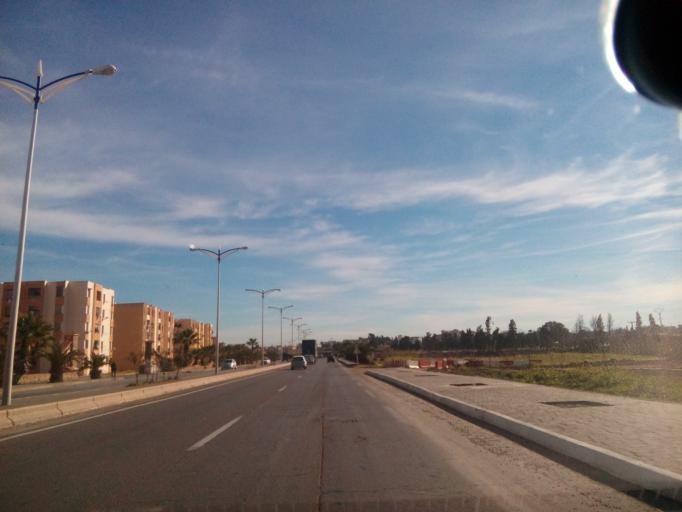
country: DZ
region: Mostaganem
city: Mostaganem
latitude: 35.9121
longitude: 0.0964
